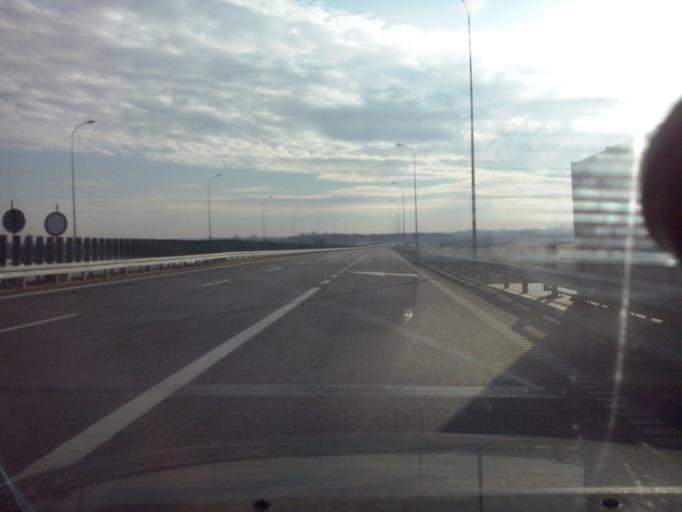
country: PL
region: Subcarpathian Voivodeship
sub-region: Powiat rzeszowski
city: Rudna Wielka
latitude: 50.1018
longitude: 21.9293
